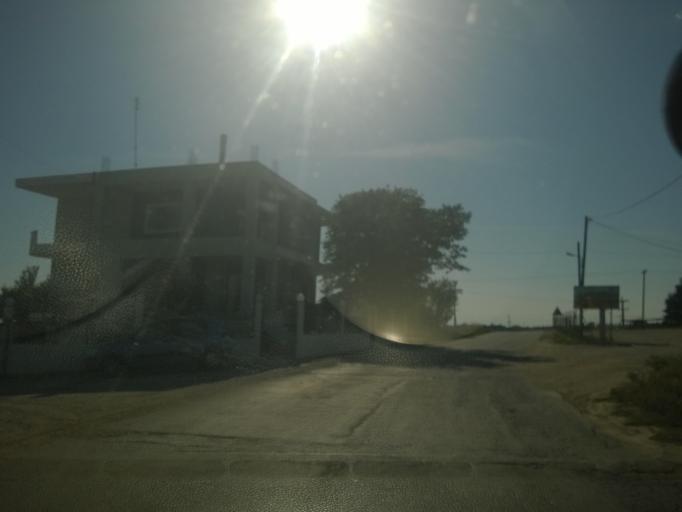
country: GR
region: Central Macedonia
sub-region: Nomos Chalkidikis
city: Nea Kallikrateia
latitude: 40.3400
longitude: 23.0598
